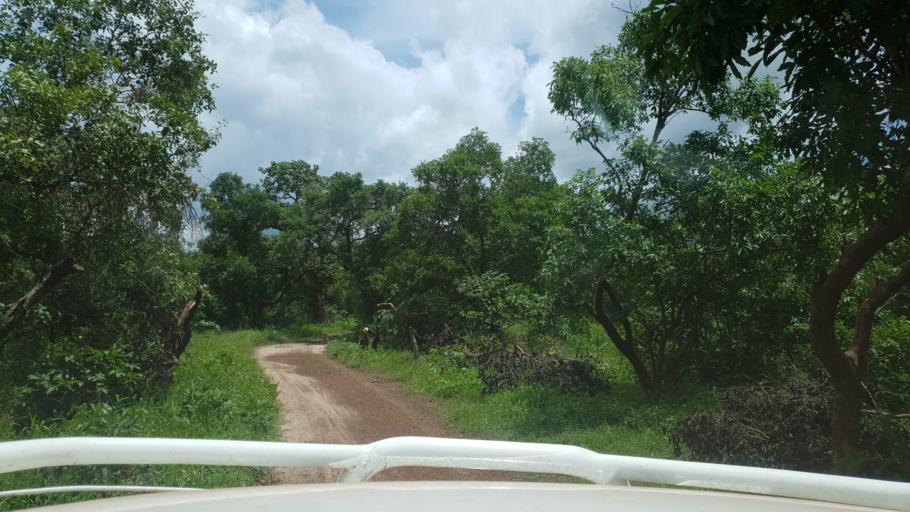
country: ML
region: Koulikoro
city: Banamba
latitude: 13.1975
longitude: -7.3265
